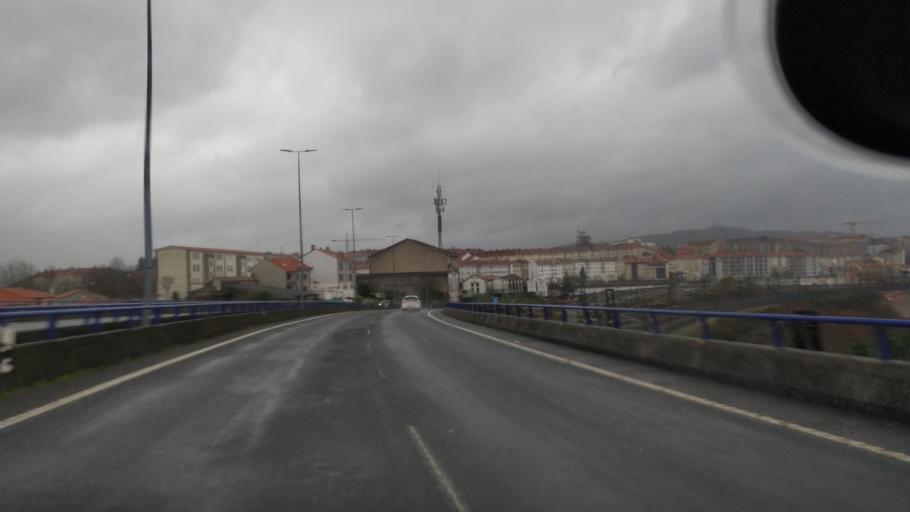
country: ES
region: Galicia
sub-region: Provincia da Coruna
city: Santiago de Compostela
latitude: 42.8633
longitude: -8.5506
